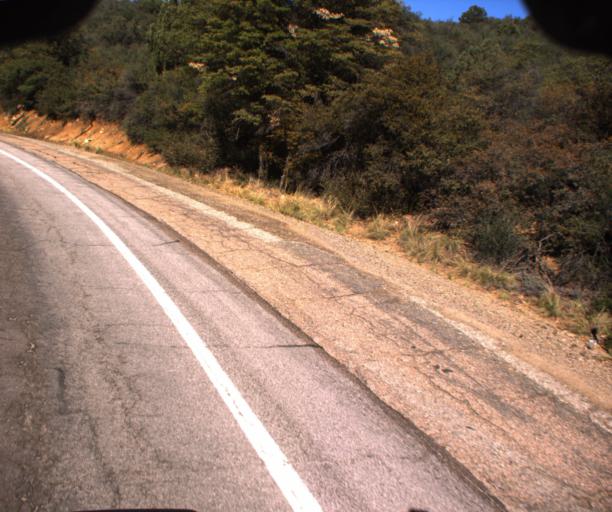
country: US
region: Arizona
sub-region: Yavapai County
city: Prescott
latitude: 34.4540
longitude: -112.5335
